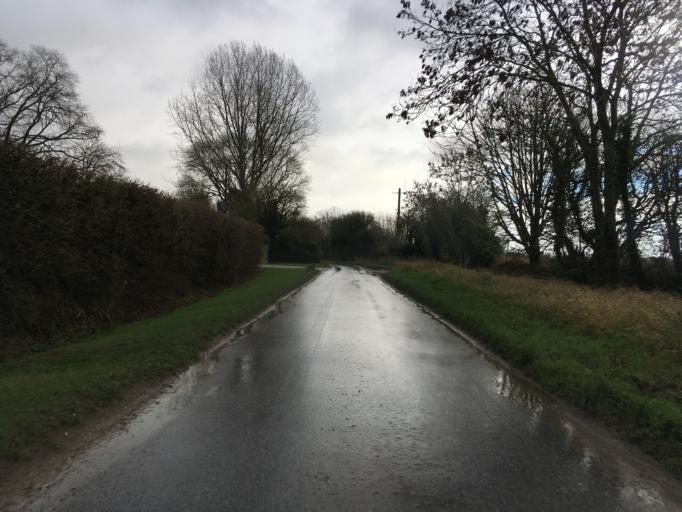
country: GB
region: England
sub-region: Wiltshire
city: Hankerton
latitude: 51.6348
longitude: -2.0866
